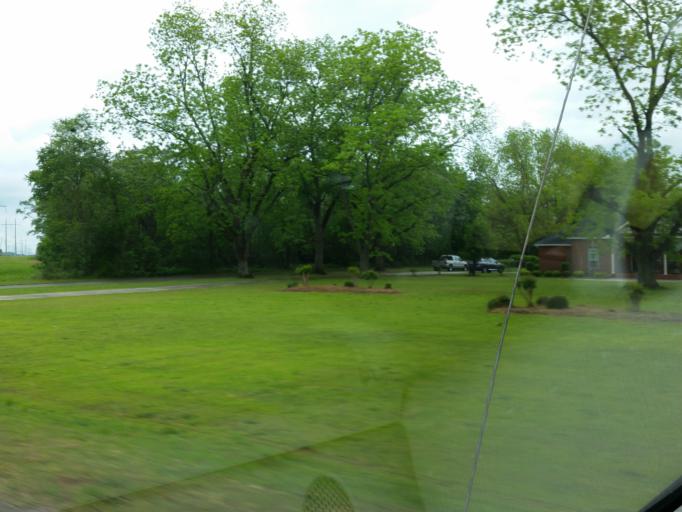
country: US
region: Georgia
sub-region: Peach County
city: Byron
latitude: 32.6517
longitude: -83.7867
